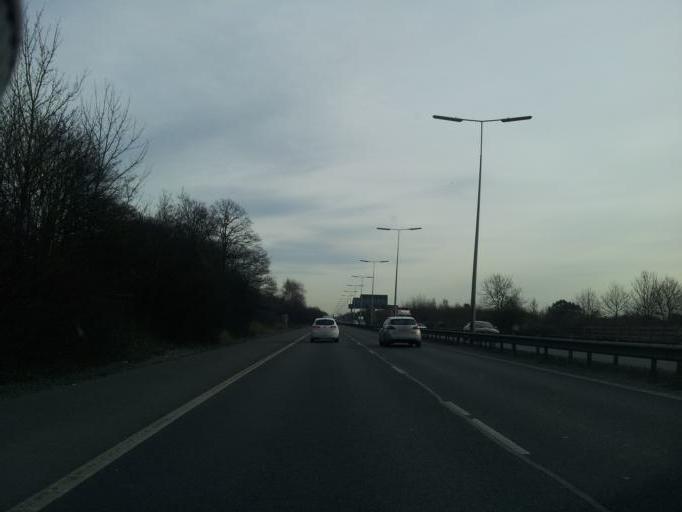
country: GB
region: England
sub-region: Hertfordshire
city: Hatfield
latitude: 51.7469
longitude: -0.2425
